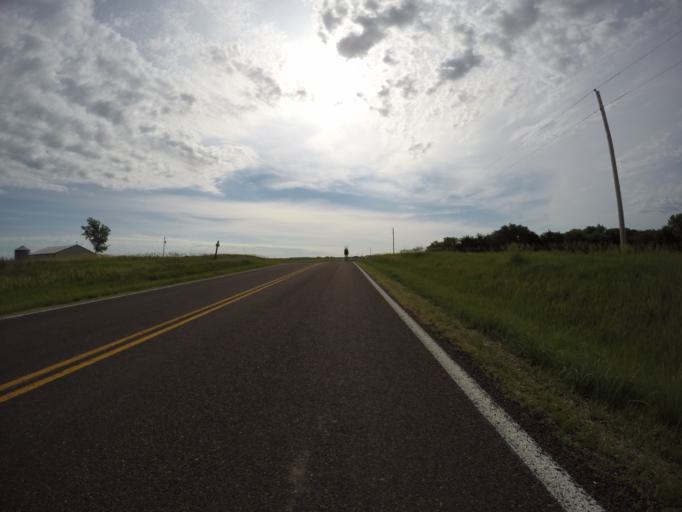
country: US
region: Kansas
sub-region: Republic County
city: Belleville
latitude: 39.7124
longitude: -97.3466
